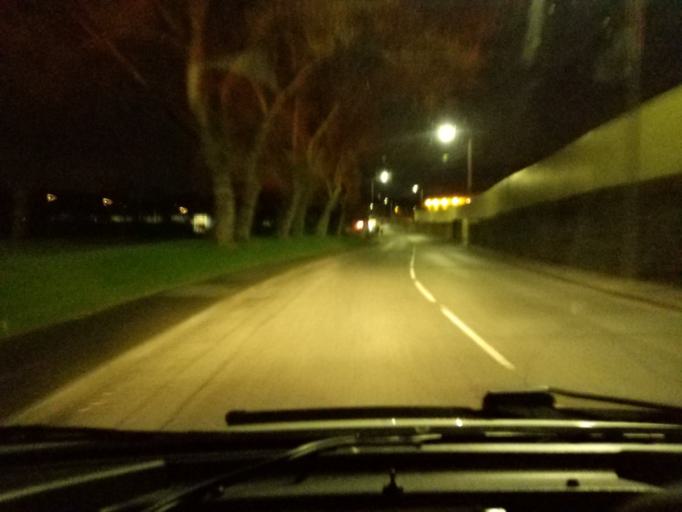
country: GB
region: England
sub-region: St. Helens
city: St Helens
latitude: 53.4628
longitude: -2.7414
